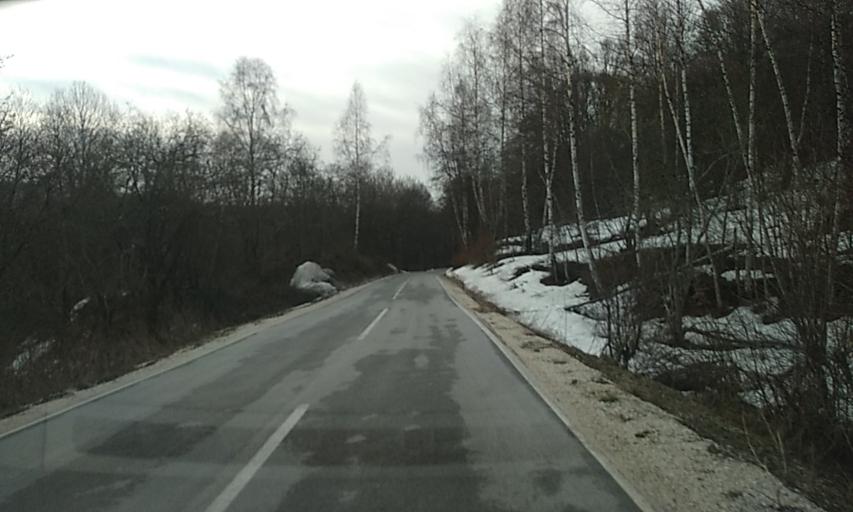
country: RS
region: Central Serbia
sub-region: Jablanicki Okrug
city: Crna Trava
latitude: 42.6695
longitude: 22.3760
